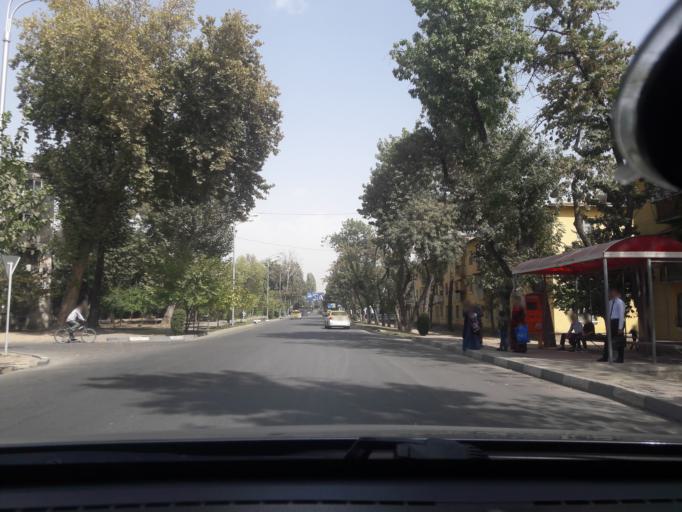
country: TJ
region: Dushanbe
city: Dushanbe
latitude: 38.5659
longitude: 68.7637
